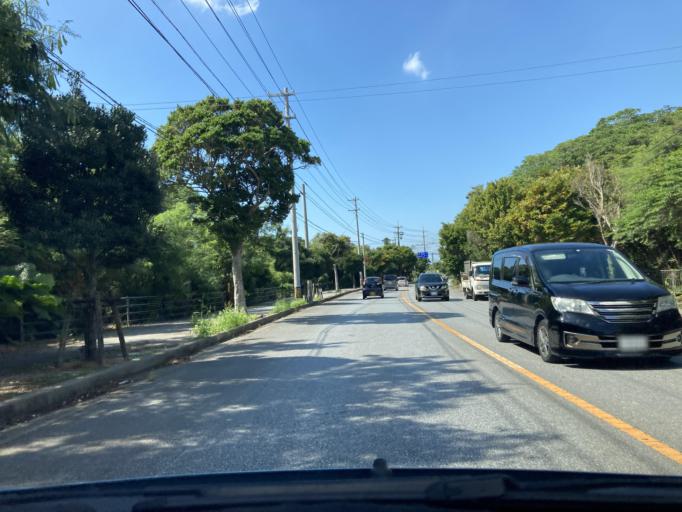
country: JP
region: Okinawa
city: Ginowan
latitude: 26.2460
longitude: 127.7593
